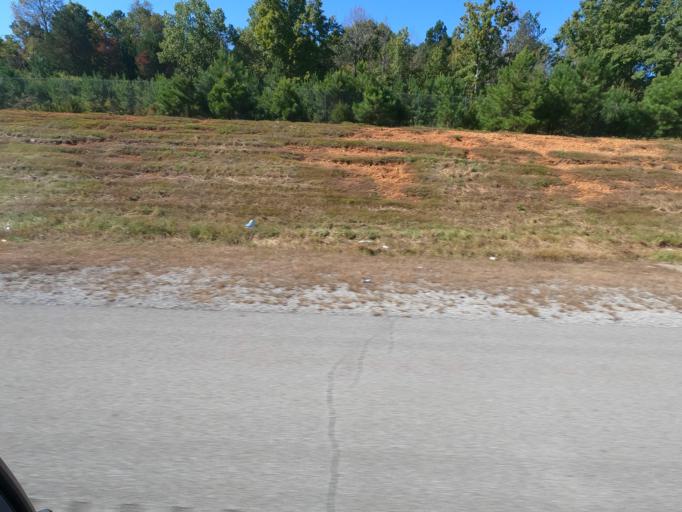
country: US
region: Tennessee
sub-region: Williamson County
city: Fairview
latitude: 35.8673
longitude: -87.0900
